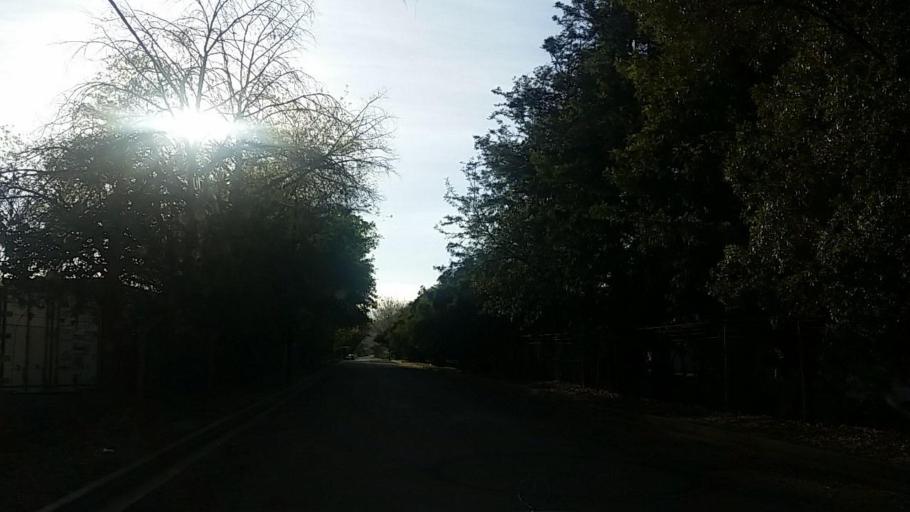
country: ZA
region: Western Cape
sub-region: Eden District Municipality
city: Knysna
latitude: -33.6550
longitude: 23.1363
